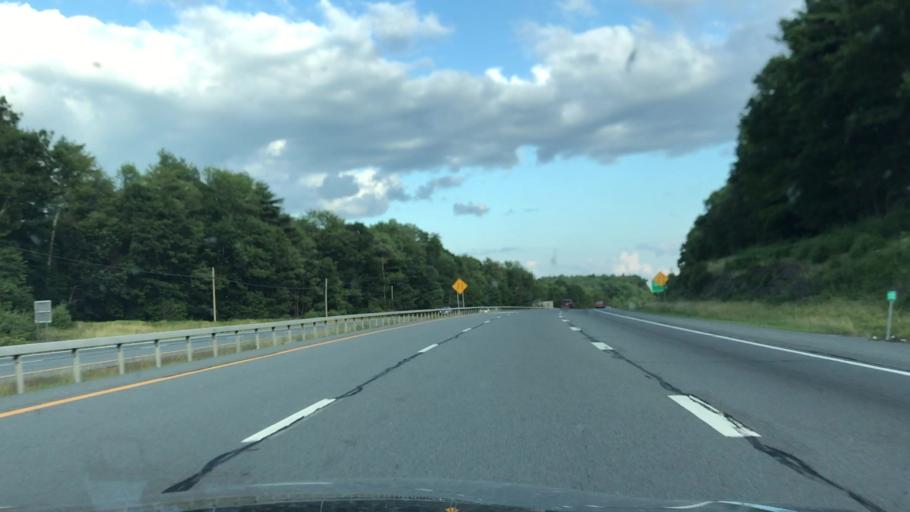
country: US
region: New York
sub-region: Sullivan County
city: Rock Hill
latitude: 41.6185
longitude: -74.5799
